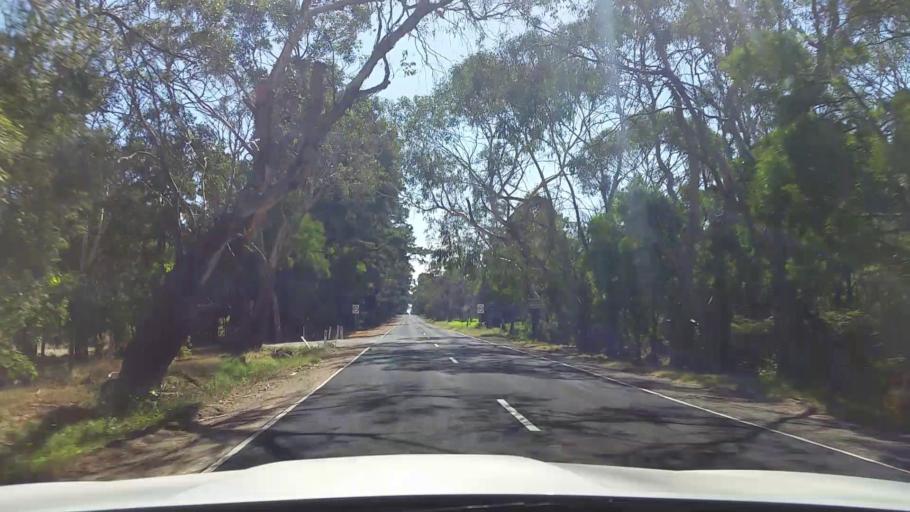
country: AU
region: Victoria
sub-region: Mornington Peninsula
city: Somerville
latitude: -38.2287
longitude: 145.1529
